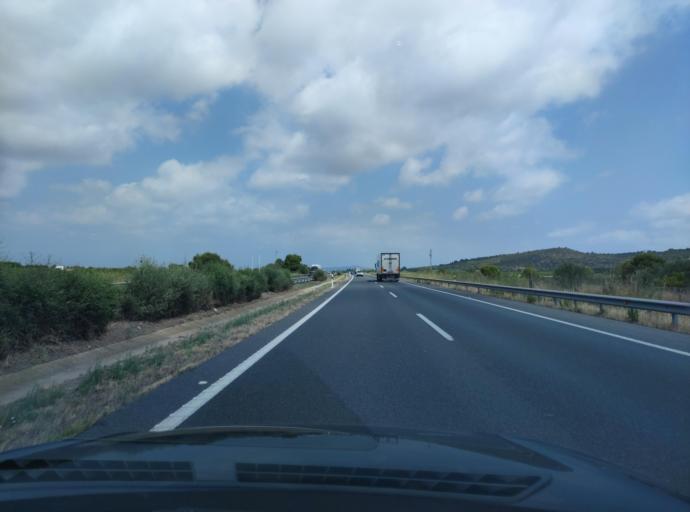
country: ES
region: Valencia
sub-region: Provincia de Castello
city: Vinaros
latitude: 40.4964
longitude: 0.4156
